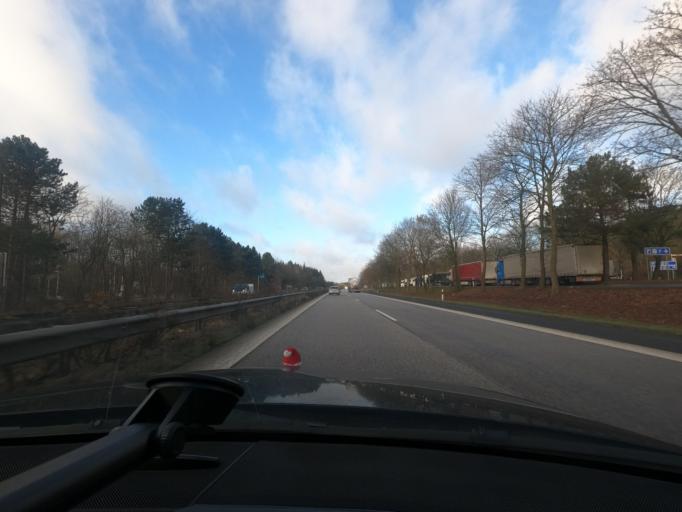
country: DE
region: Schleswig-Holstein
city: Neu Duvenstedt
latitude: 54.3644
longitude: 9.6718
